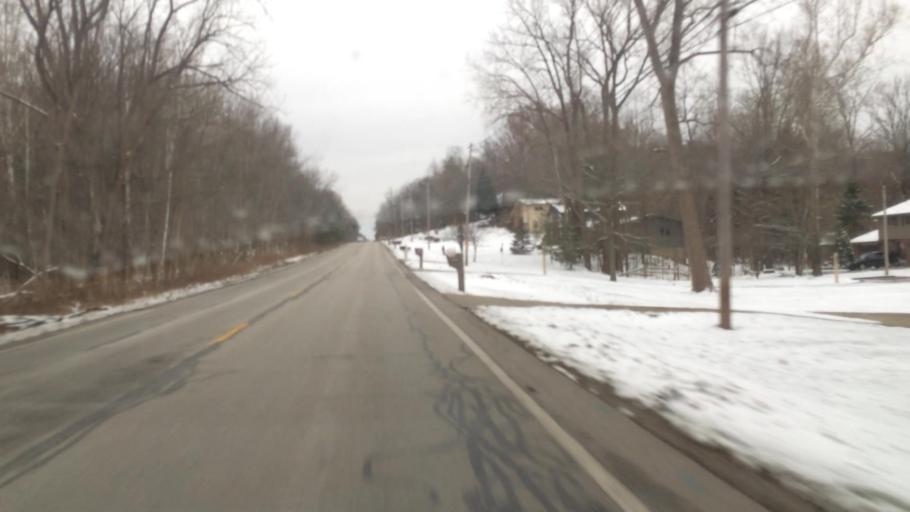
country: US
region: Ohio
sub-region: Cuyahoga County
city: Strongsville
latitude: 41.3056
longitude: -81.7853
